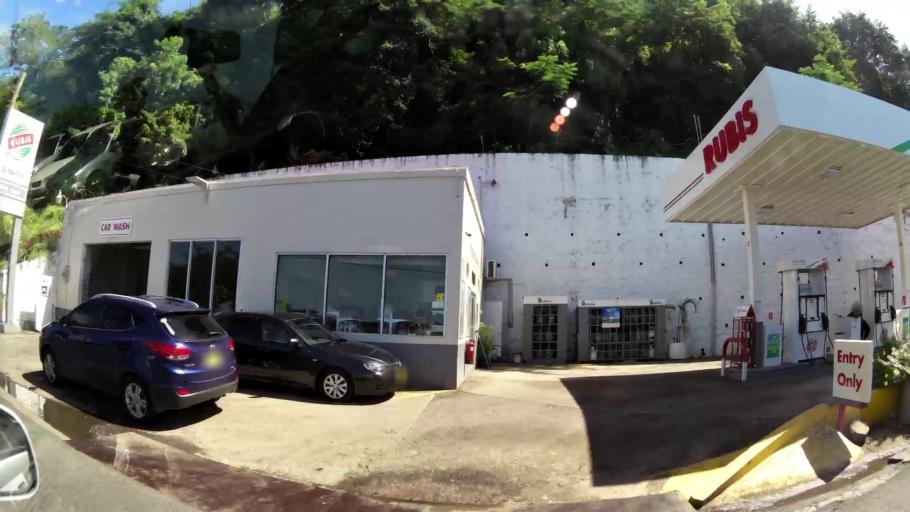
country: GD
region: Saint George
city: Saint George's
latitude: 12.0558
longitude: -61.7544
